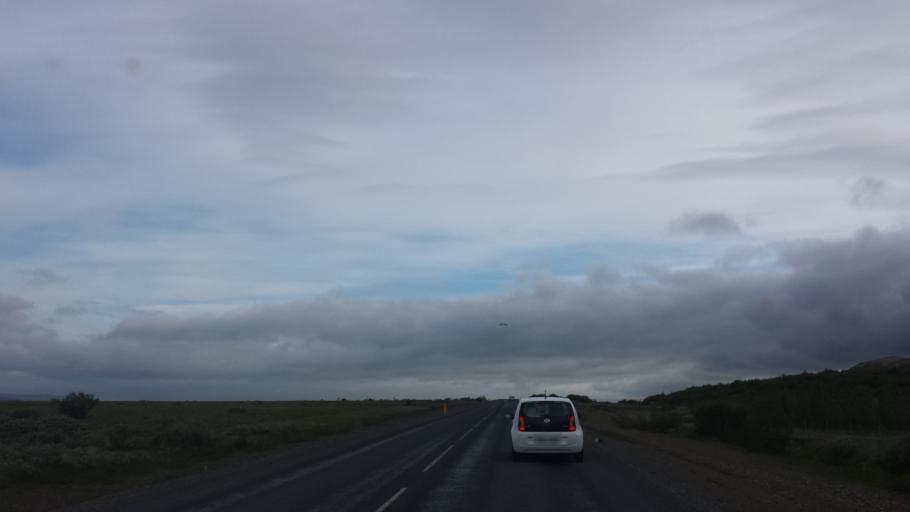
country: IS
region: South
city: Selfoss
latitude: 64.2906
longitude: -20.3375
